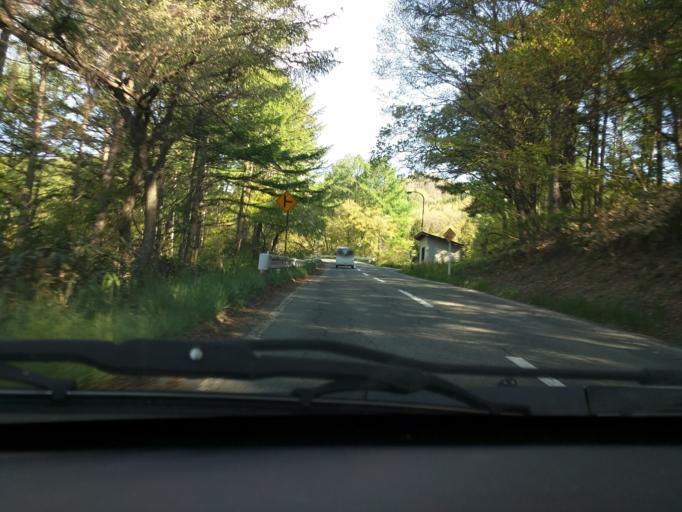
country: JP
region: Nagano
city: Nagano-shi
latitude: 36.6902
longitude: 138.1566
